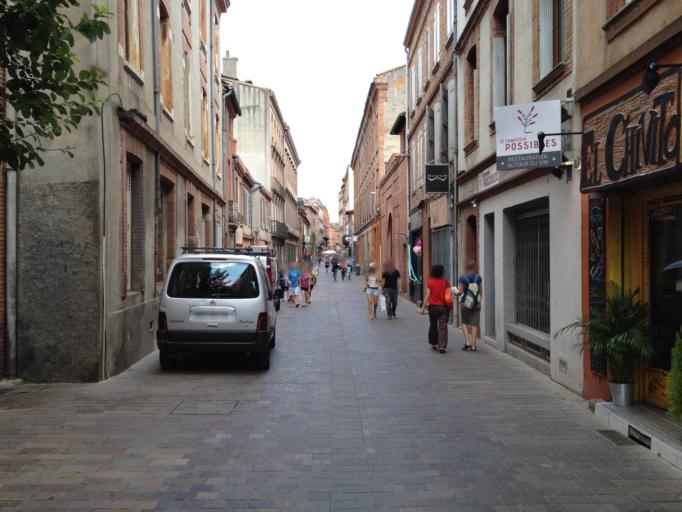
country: FR
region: Midi-Pyrenees
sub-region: Departement de la Haute-Garonne
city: Toulouse
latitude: 43.6044
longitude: 1.4395
